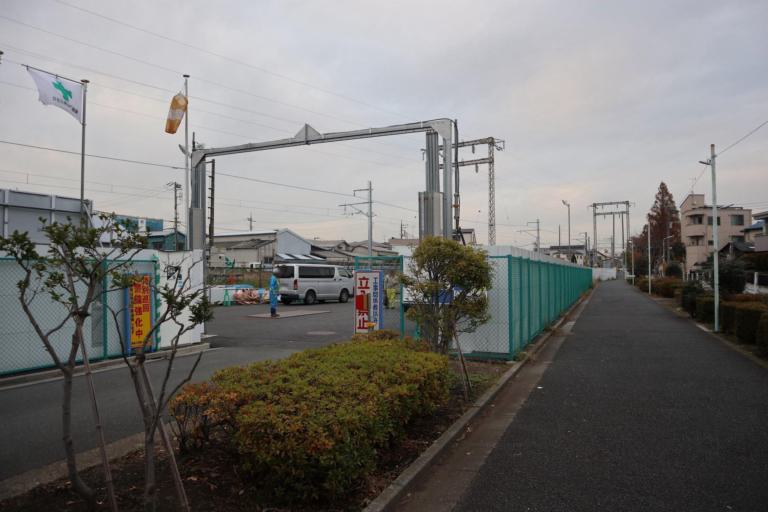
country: JP
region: Chiba
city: Matsudo
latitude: 35.7535
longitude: 139.8629
